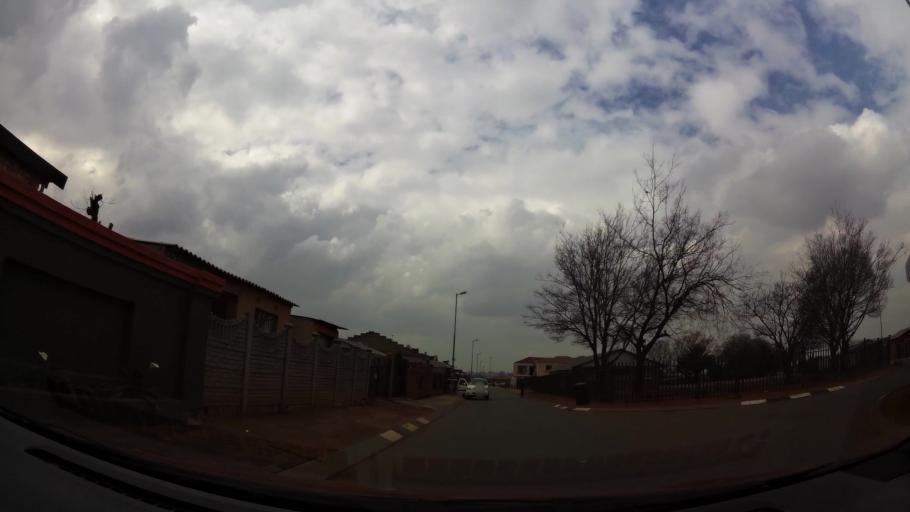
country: ZA
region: Gauteng
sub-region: City of Johannesburg Metropolitan Municipality
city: Soweto
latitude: -26.2595
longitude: 27.8299
